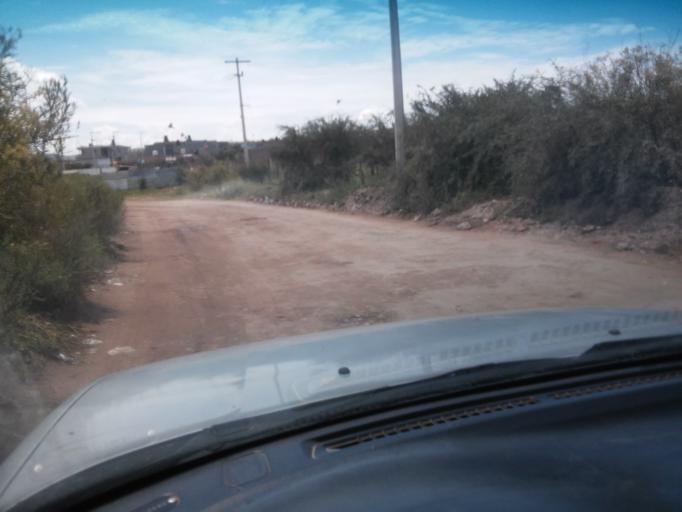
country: MX
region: Durango
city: Victoria de Durango
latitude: 23.9872
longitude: -104.7104
